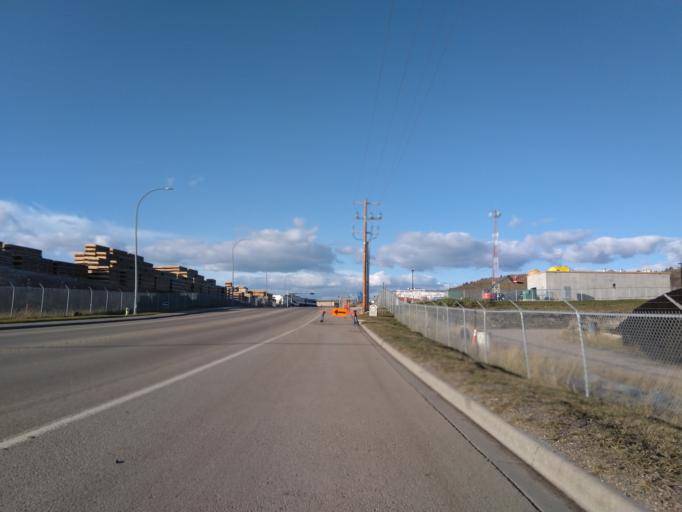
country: CA
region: Alberta
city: Cochrane
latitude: 51.1814
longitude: -114.4667
